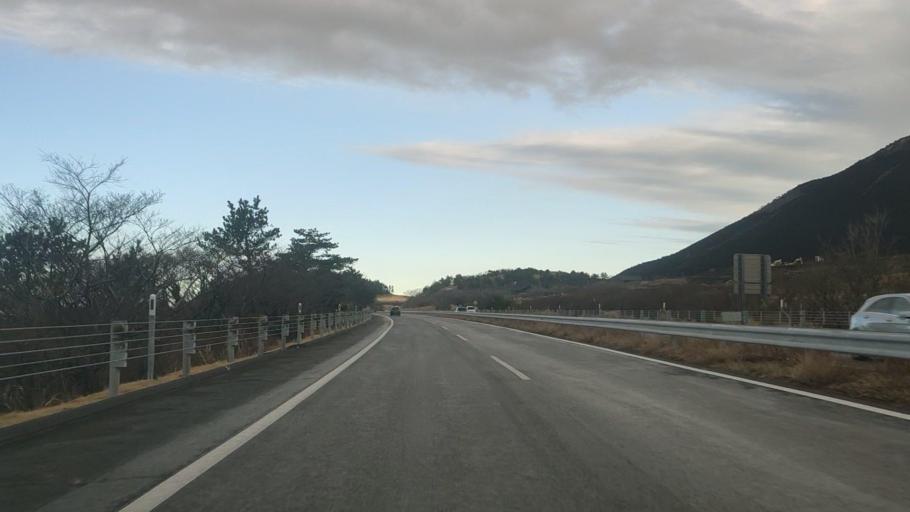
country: JP
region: Oita
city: Beppu
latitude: 33.3091
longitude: 131.4065
